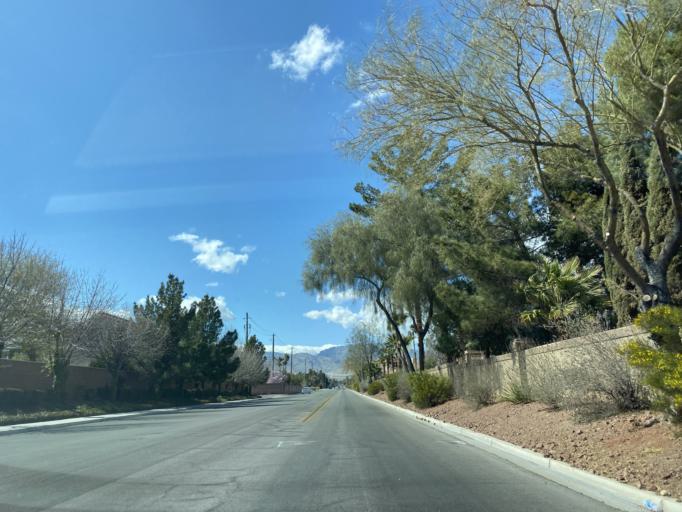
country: US
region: Nevada
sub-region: Clark County
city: Las Vegas
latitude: 36.2555
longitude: -115.2615
